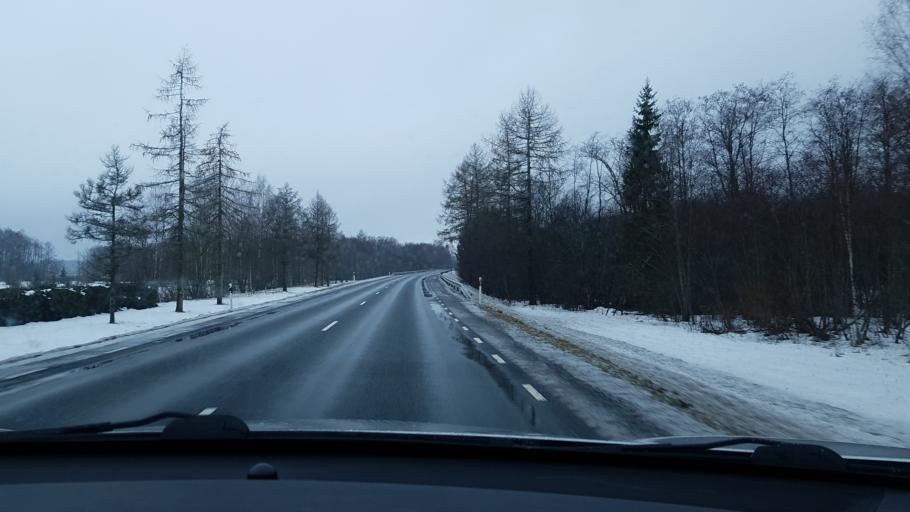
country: EE
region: Jaervamaa
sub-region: Tueri vald
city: Sarevere
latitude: 58.7997
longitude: 25.2528
